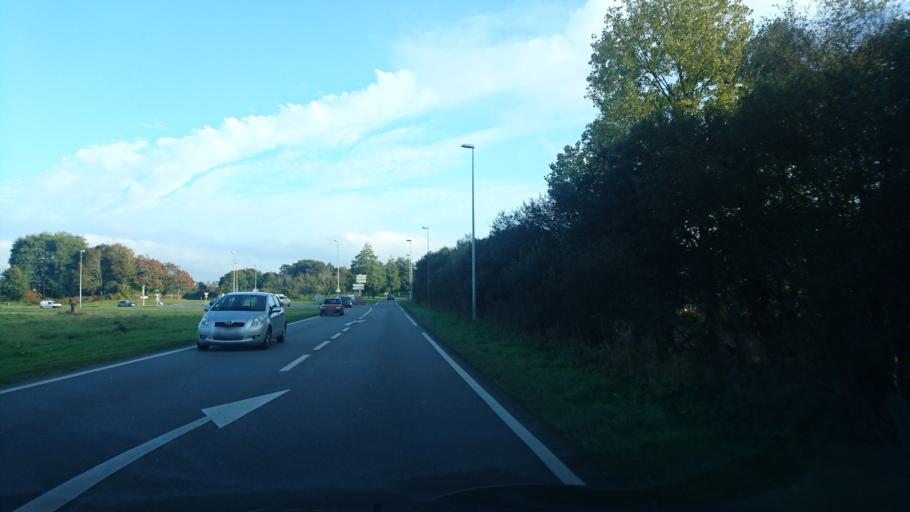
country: FR
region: Brittany
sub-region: Departement du Finistere
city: Gouesnou
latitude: 48.4469
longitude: -4.4665
